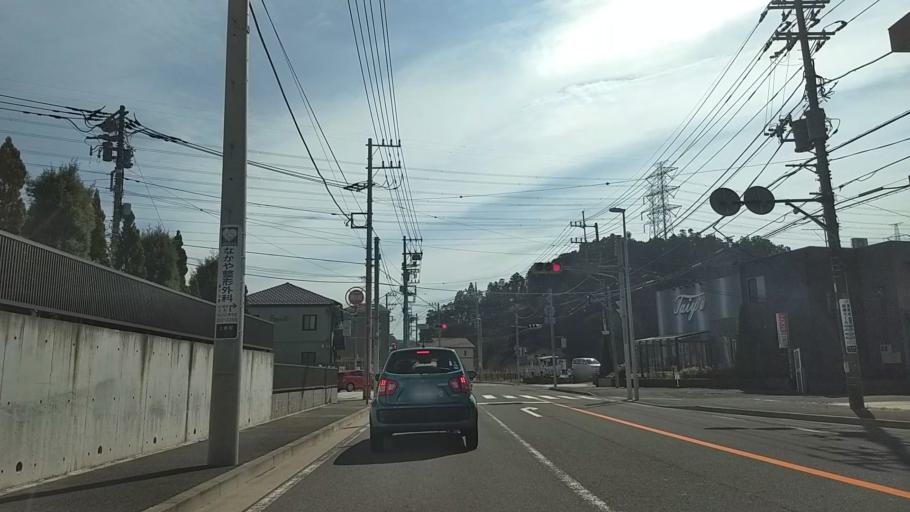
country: JP
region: Kanagawa
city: Kamakura
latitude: 35.3637
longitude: 139.5725
